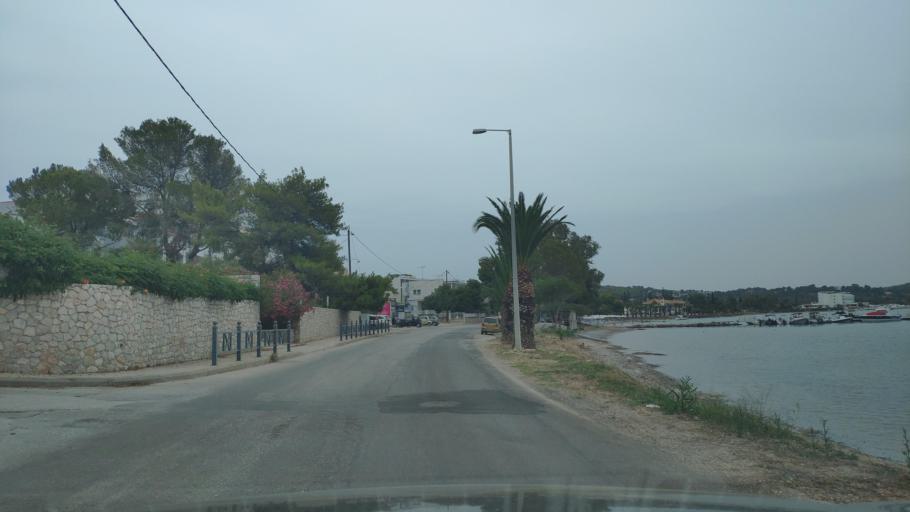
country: GR
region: Peloponnese
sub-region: Nomos Argolidos
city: Porto Cheli
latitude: 37.3252
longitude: 23.1541
